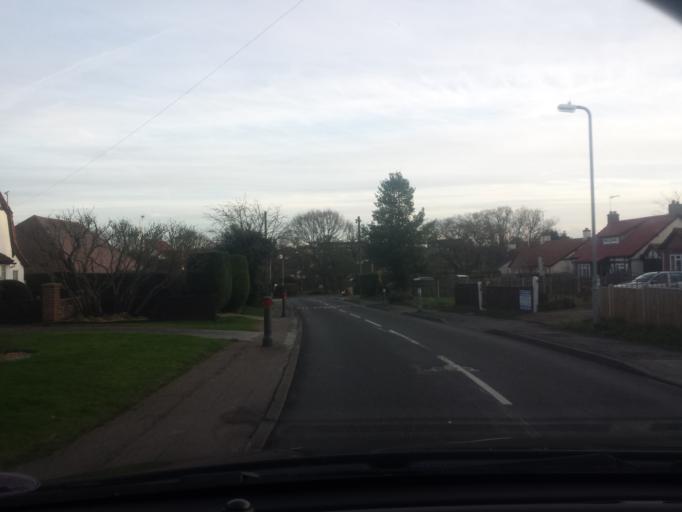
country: GB
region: England
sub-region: Essex
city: Clacton-on-Sea
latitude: 51.8060
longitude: 1.1765
